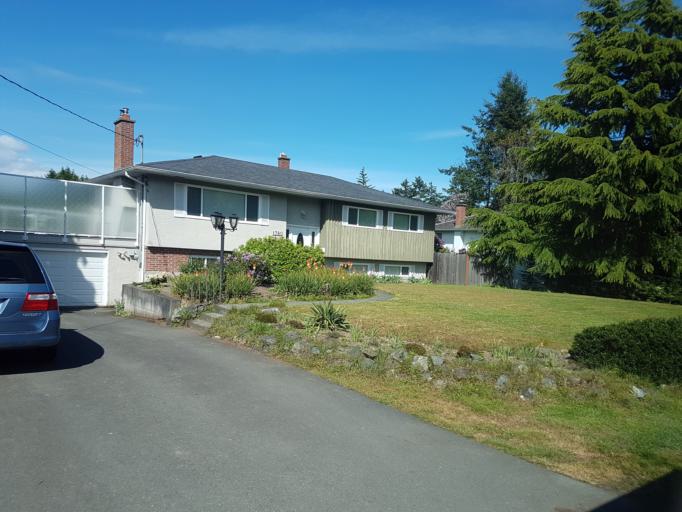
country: CA
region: British Columbia
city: Oak Bay
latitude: 48.4898
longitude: -123.3188
